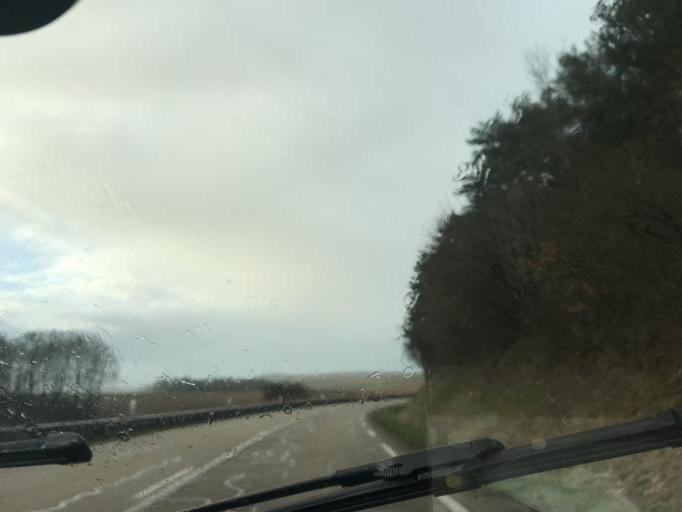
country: FR
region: Bourgogne
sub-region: Departement de l'Yonne
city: Fontenailles
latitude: 47.6315
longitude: 3.4911
